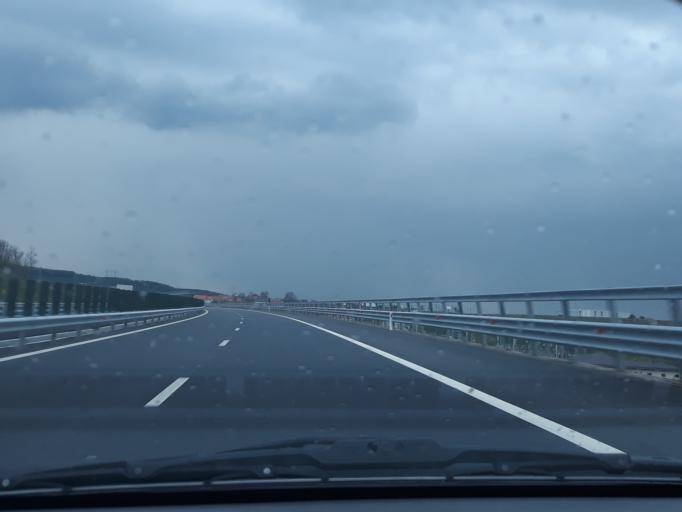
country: RO
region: Mures
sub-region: Comuna Sanpaul
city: Valea Izvoarelor
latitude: 46.4545
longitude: 24.3808
